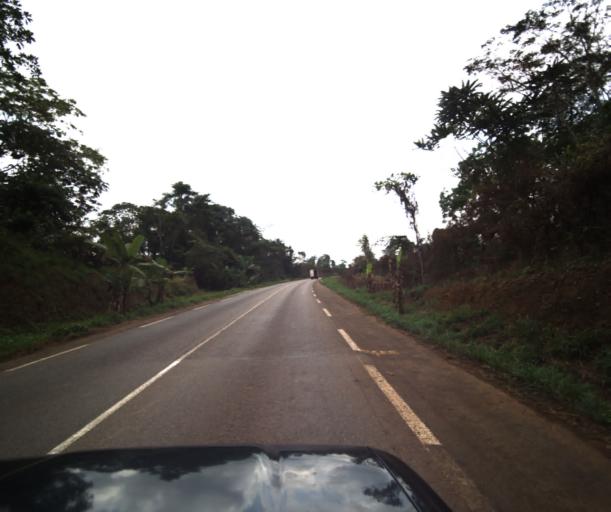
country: CM
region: Centre
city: Eseka
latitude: 3.8705
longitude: 10.6571
